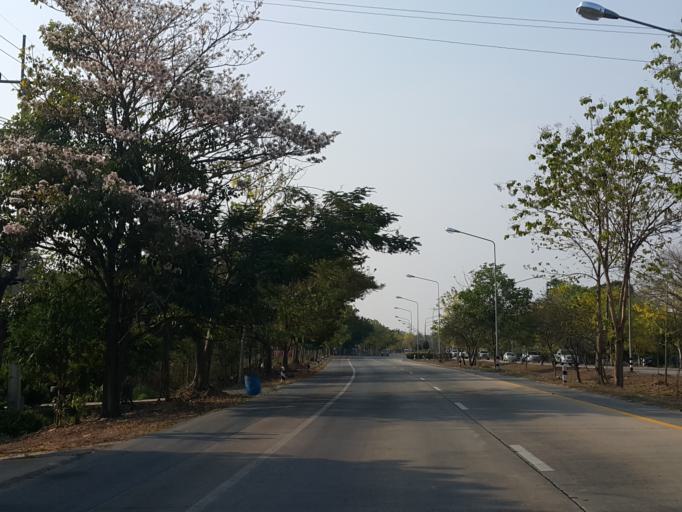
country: TH
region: Suphan Buri
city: Sam Chuk
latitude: 14.7798
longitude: 100.0892
